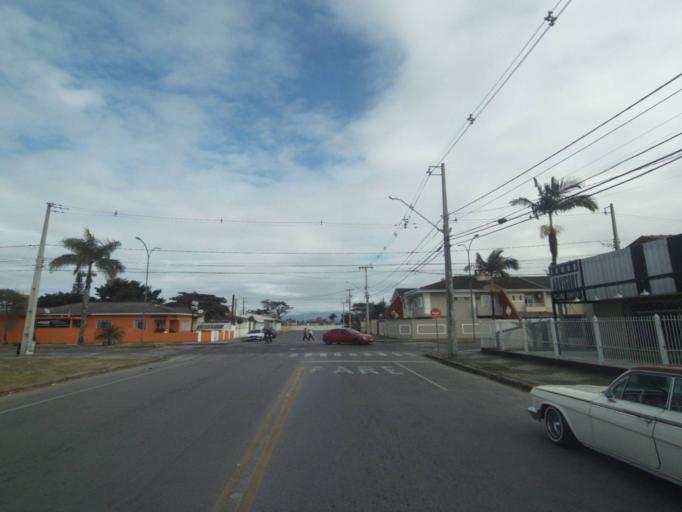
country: BR
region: Parana
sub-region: Paranagua
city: Paranagua
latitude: -25.5192
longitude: -48.5152
